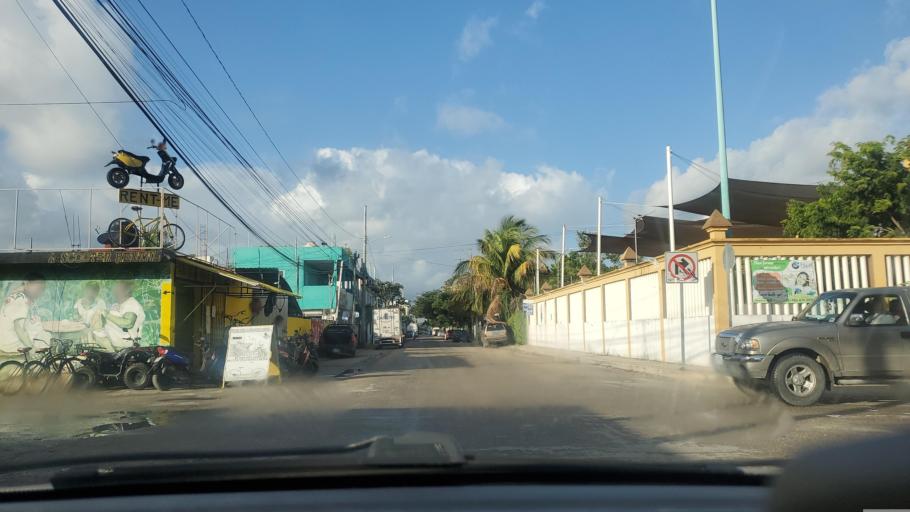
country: MX
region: Quintana Roo
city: Tulum
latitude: 20.2124
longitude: -87.4542
